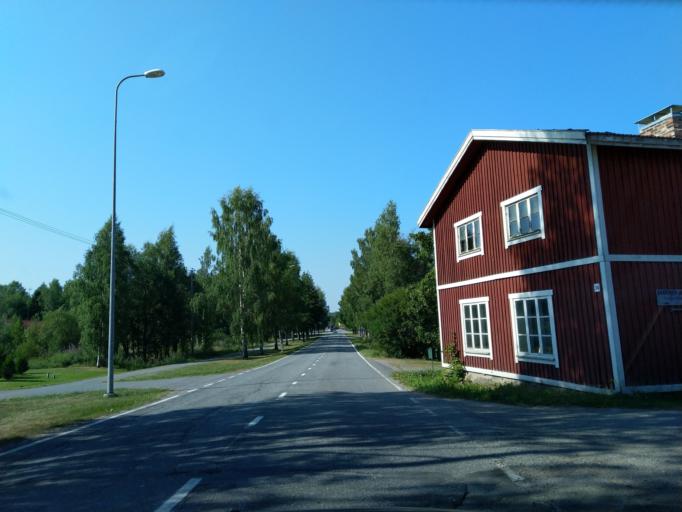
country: FI
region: Satakunta
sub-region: Pori
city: Pomarkku
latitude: 61.7001
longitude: 22.0170
